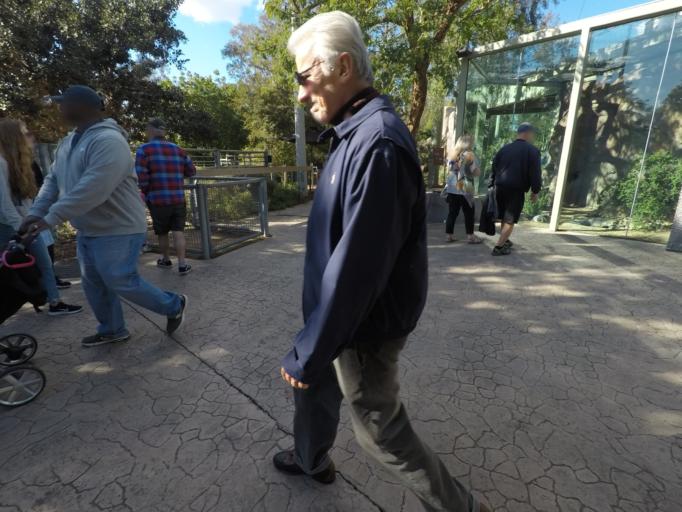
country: US
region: California
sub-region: San Diego County
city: San Diego
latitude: 32.7390
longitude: -117.1517
